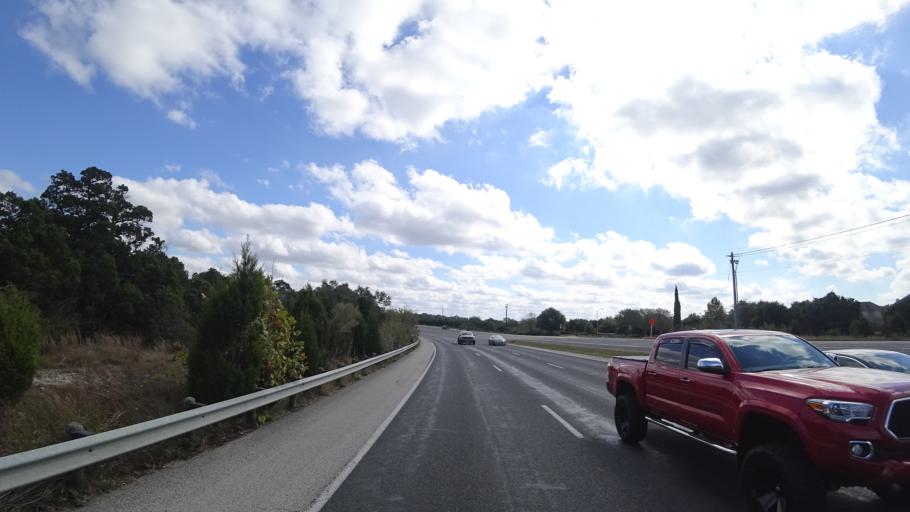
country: US
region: Texas
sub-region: Travis County
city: Barton Creek
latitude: 30.2582
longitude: -97.8824
